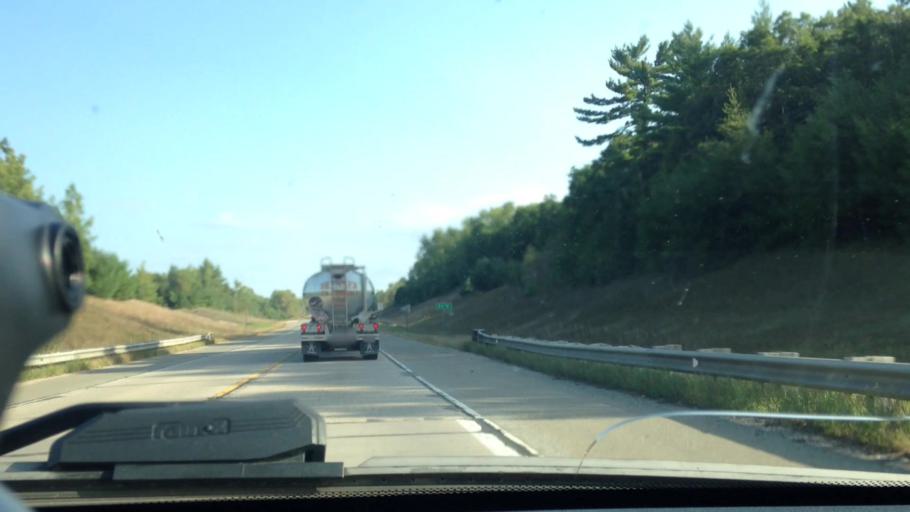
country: US
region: Wisconsin
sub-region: Marinette County
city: Niagara
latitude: 45.6490
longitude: -87.9646
